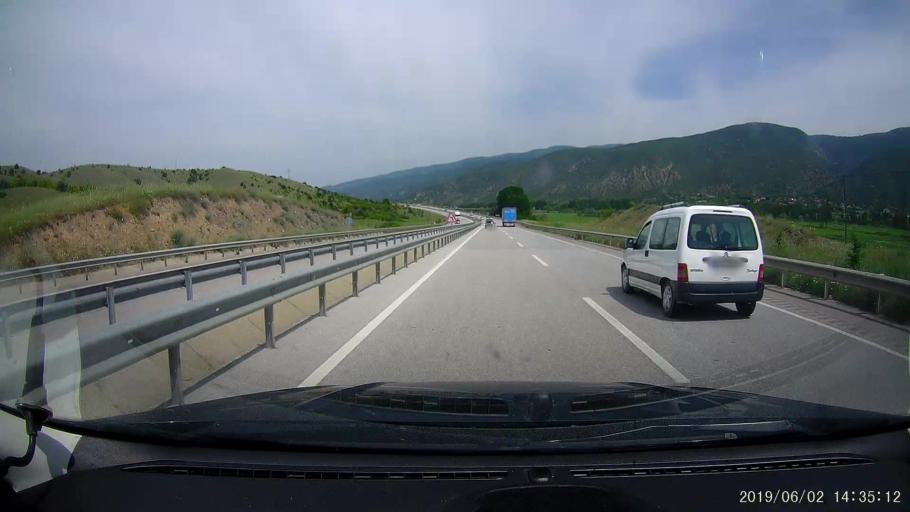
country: TR
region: Kastamonu
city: Tosya
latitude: 41.0402
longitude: 34.2096
